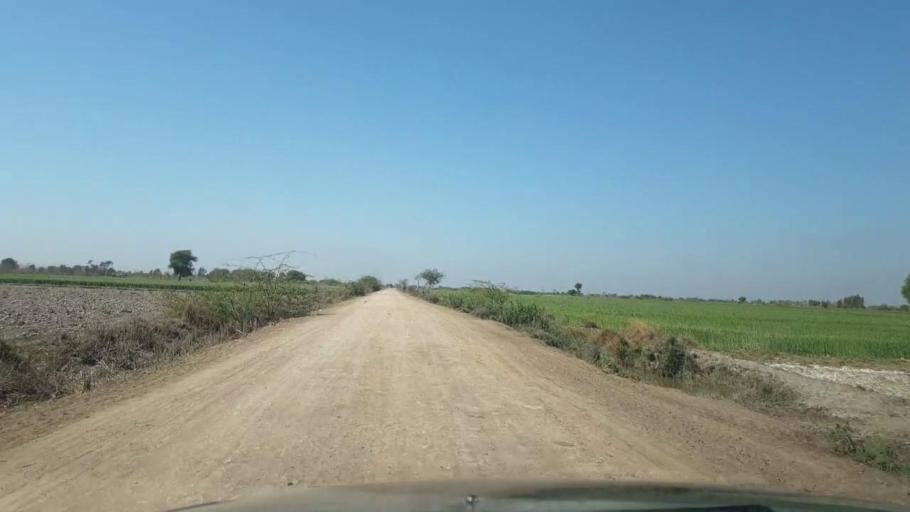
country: PK
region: Sindh
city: Mirpur Khas
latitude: 25.5860
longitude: 69.0632
